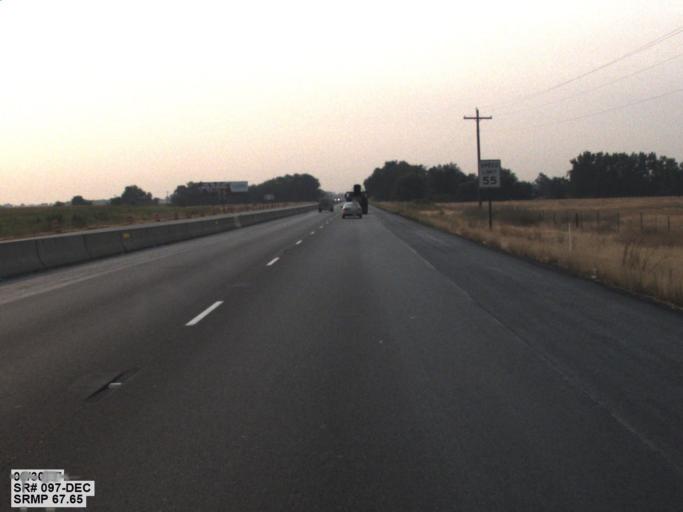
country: US
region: Washington
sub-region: Yakima County
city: Wapato
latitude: 46.4309
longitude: -120.4153
